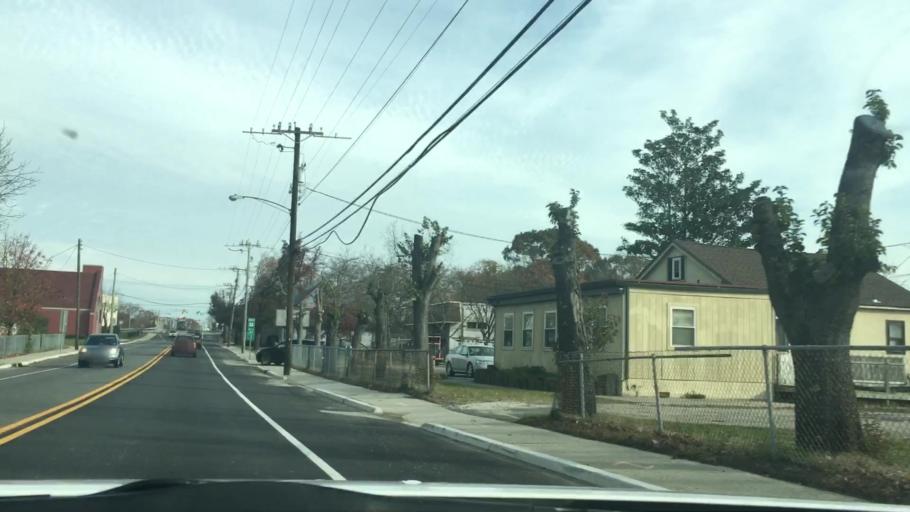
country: US
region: New Jersey
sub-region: Atlantic County
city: Pleasantville
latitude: 39.3994
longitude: -74.5258
